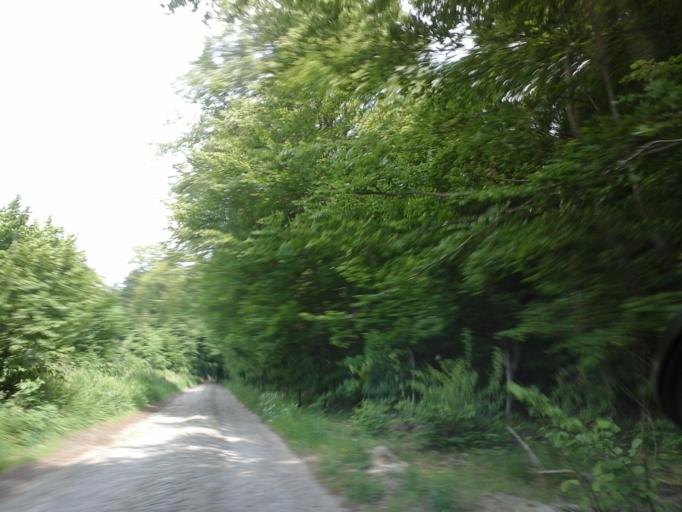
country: PL
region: West Pomeranian Voivodeship
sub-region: Powiat choszczenski
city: Drawno
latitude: 53.1717
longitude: 15.7934
